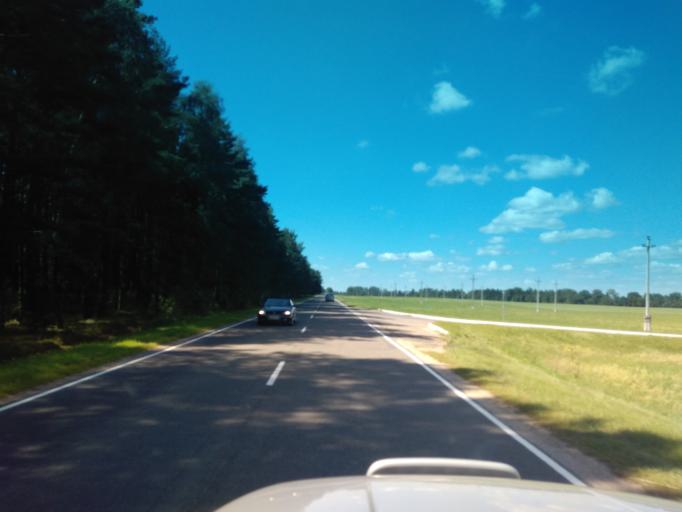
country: BY
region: Minsk
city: Stan'kava
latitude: 53.6248
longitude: 27.2772
